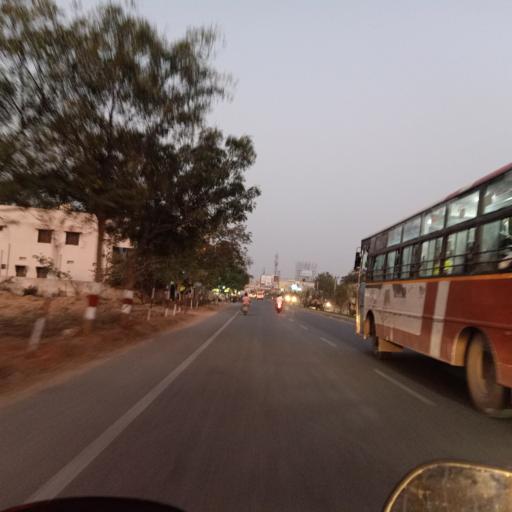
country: IN
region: Telangana
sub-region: Rangareddi
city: Secunderabad
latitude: 17.5629
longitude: 78.5495
